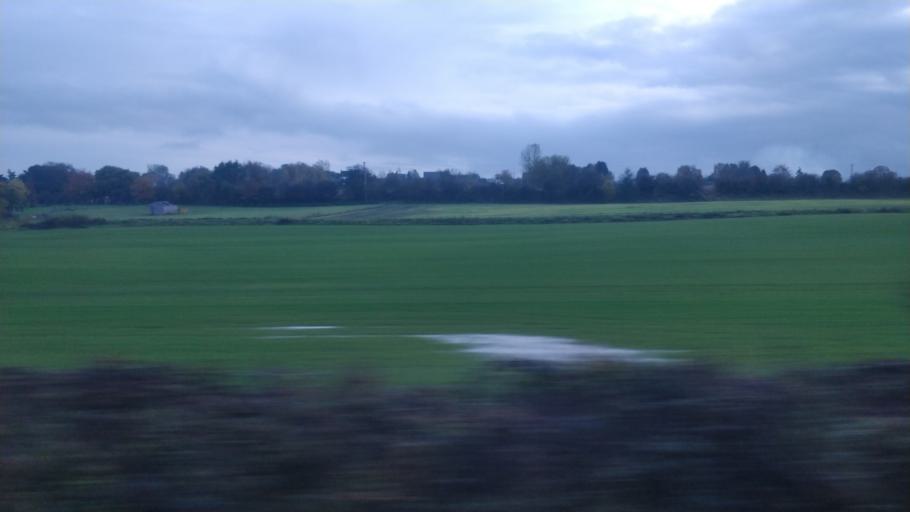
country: GB
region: England
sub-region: Lancashire
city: Parbold
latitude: 53.5937
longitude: -2.7851
